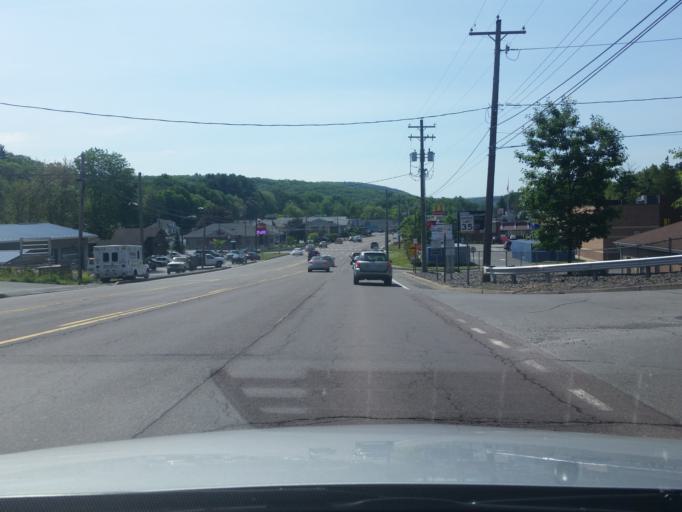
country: US
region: Pennsylvania
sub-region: Luzerne County
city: Shavertown
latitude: 41.3243
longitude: -75.9438
